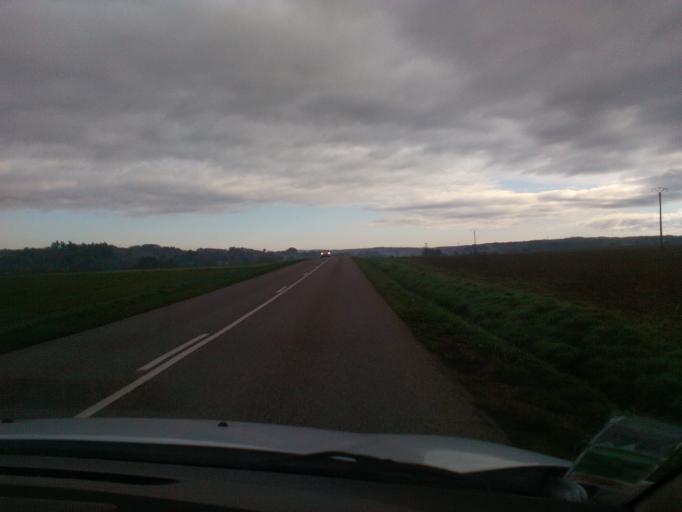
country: FR
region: Lorraine
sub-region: Departement des Vosges
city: Jeanmenil
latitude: 48.3450
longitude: 6.6637
